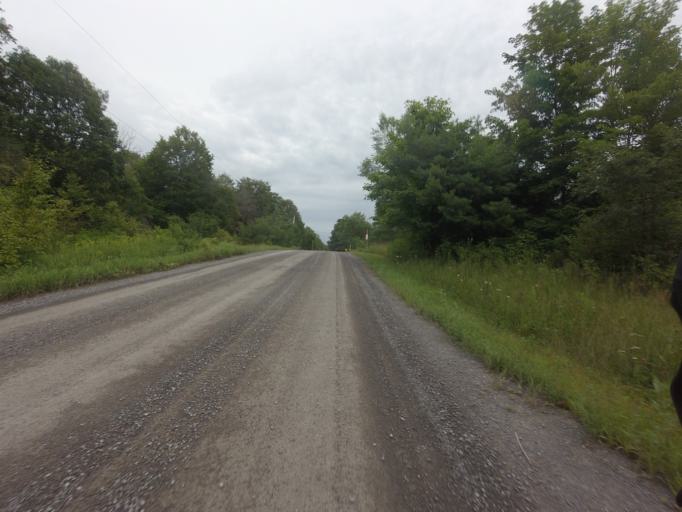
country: CA
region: Ontario
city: Carleton Place
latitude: 45.1523
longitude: -76.2586
